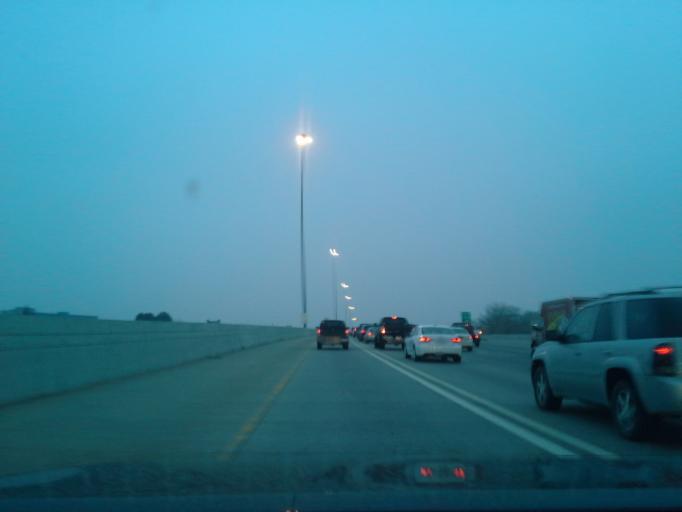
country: US
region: Utah
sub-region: Salt Lake County
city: Murray
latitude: 40.6595
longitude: -111.9013
